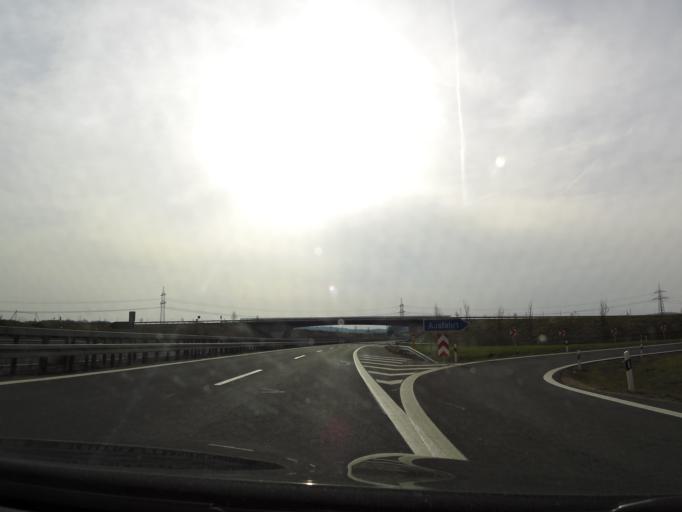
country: DE
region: Bavaria
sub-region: Upper Franconia
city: Rodental
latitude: 50.2957
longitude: 11.0029
